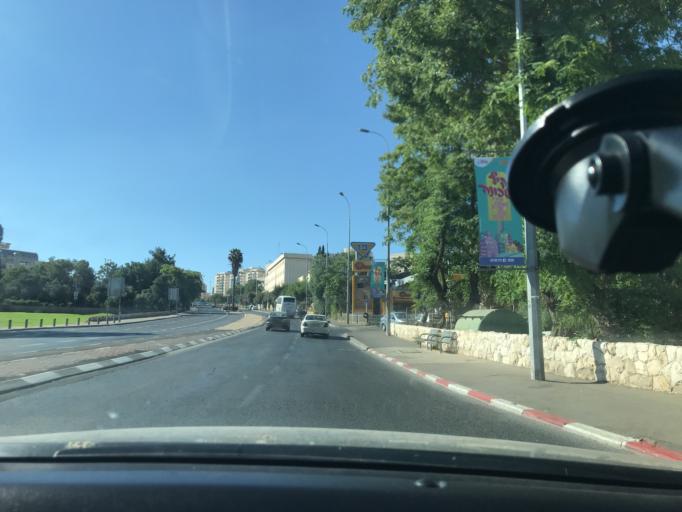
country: IL
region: Jerusalem
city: West Jerusalem
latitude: 31.7831
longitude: 35.2085
